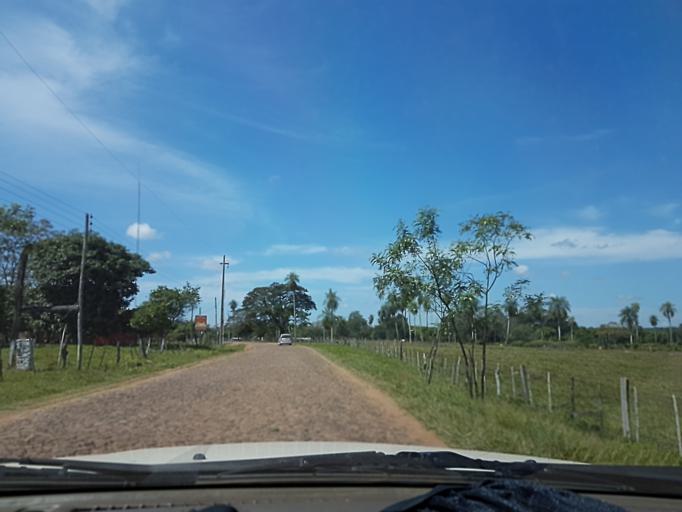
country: PY
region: Cordillera
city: Arroyos y Esteros
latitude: -24.9875
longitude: -57.2022
